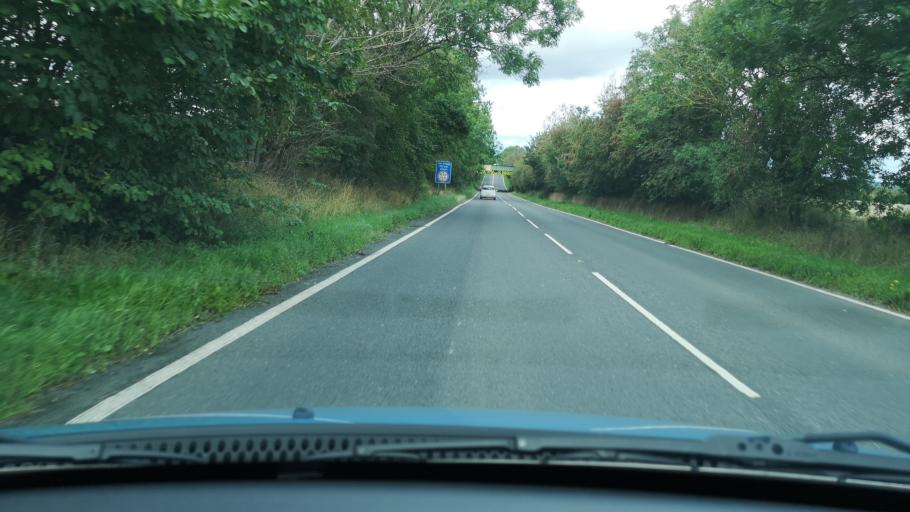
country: GB
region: England
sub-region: City and Borough of Wakefield
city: Badsworth
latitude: 53.6287
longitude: -1.3183
